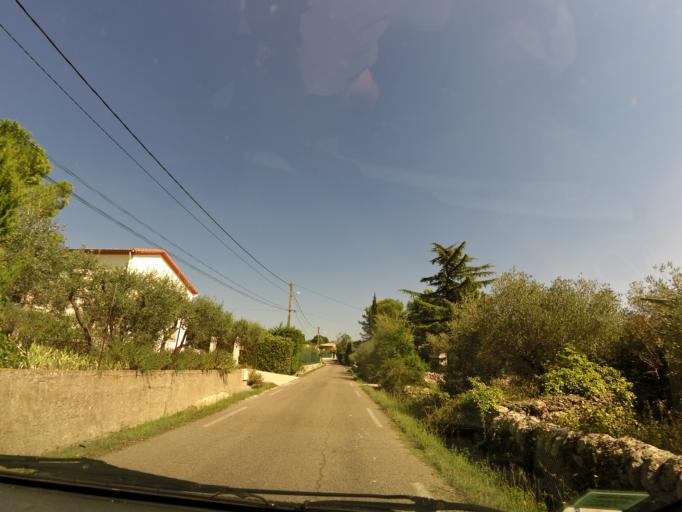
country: FR
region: Languedoc-Roussillon
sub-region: Departement du Gard
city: Villevieille
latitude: 43.7932
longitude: 4.0999
